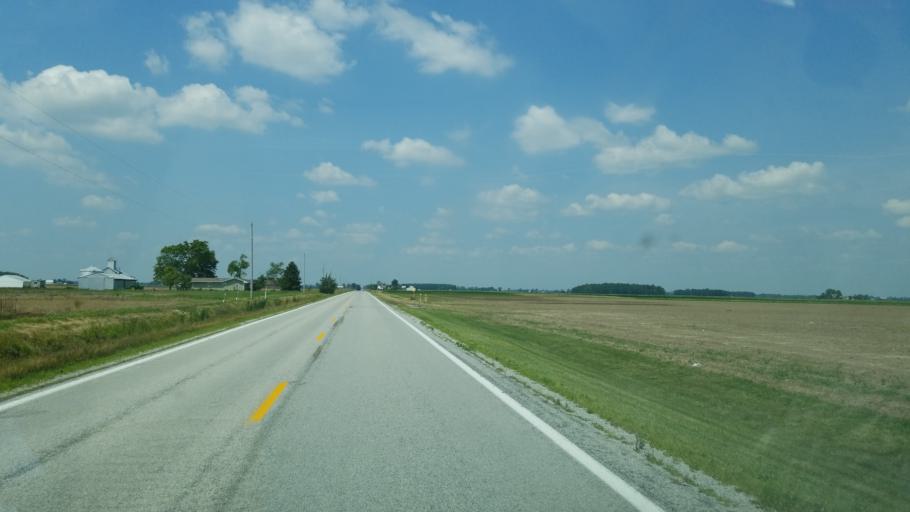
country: US
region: Ohio
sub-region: Henry County
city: Deshler
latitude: 41.2834
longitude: -83.9859
